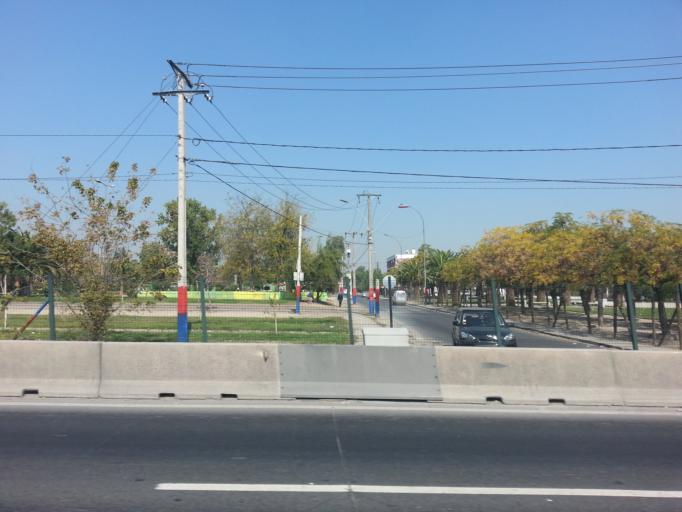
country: CL
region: Santiago Metropolitan
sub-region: Provincia de Santiago
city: La Pintana
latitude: -33.5412
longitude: -70.6444
